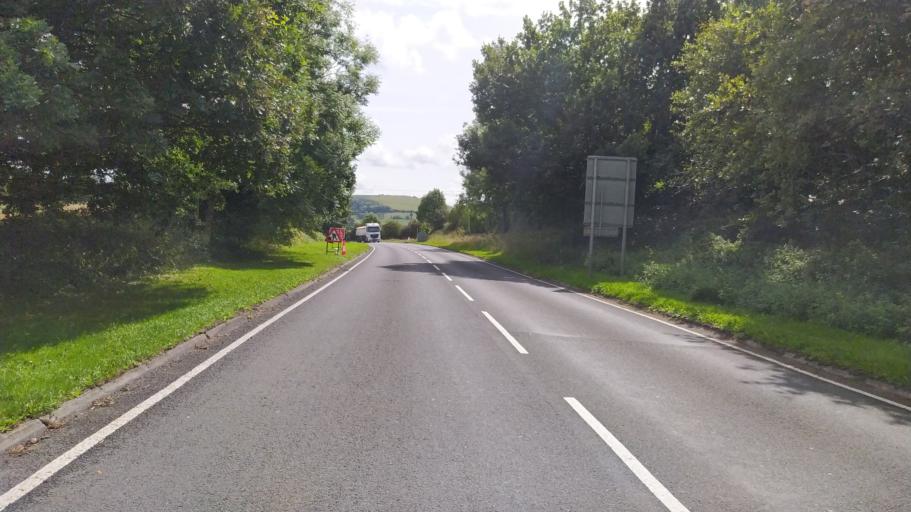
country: GB
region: England
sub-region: Dorset
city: Shaftesbury
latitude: 51.0003
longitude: -2.1851
